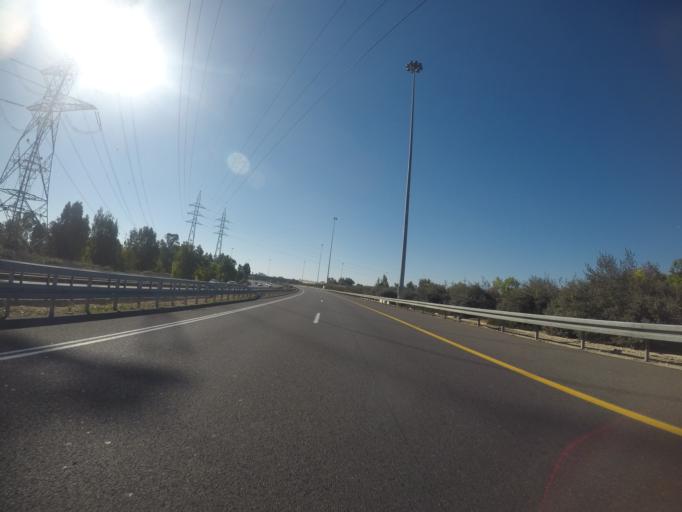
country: IL
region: Southern District
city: Ashdod
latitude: 31.7804
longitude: 34.6690
